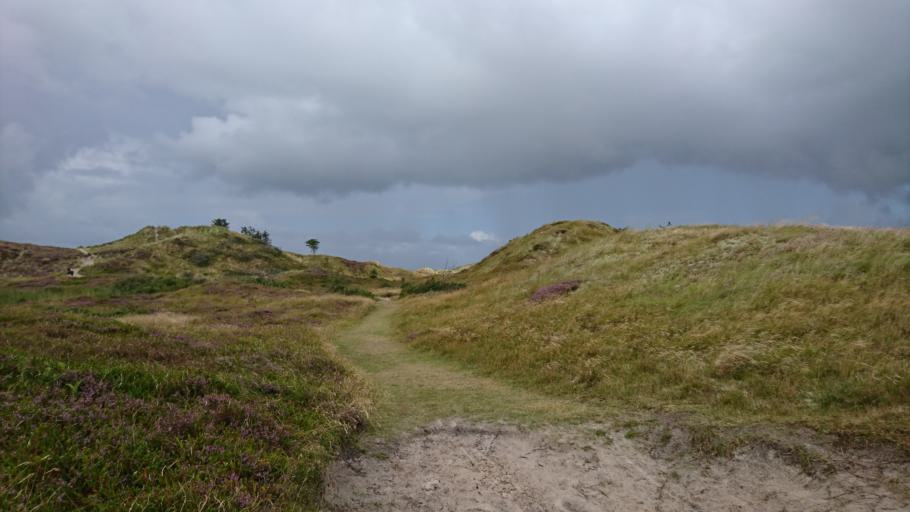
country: DK
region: South Denmark
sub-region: Fano Kommune
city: Nordby
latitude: 55.3790
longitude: 8.4184
